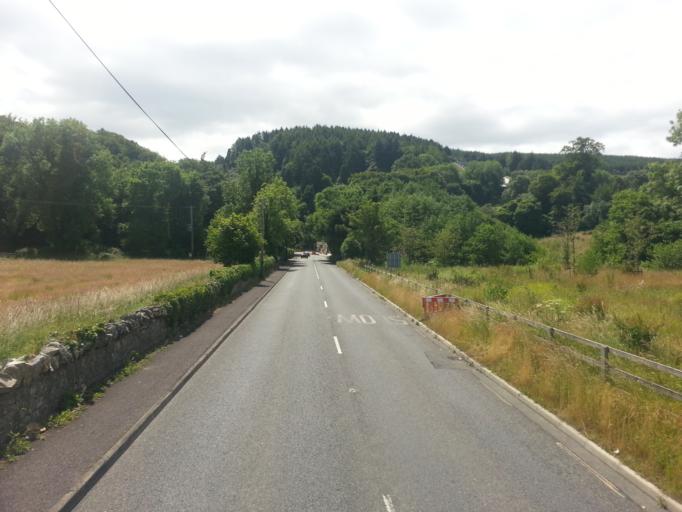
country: IE
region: Leinster
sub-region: Wicklow
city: Enniskerry
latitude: 53.2224
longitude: -6.1816
